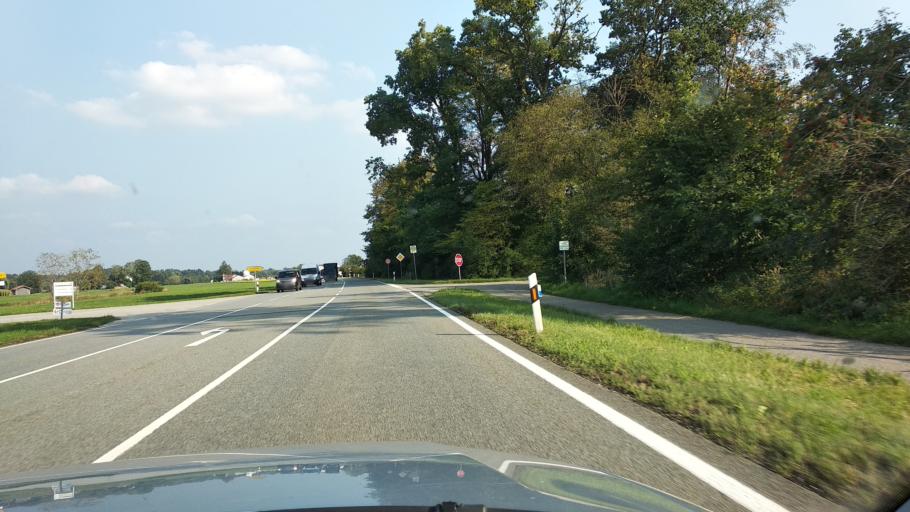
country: DE
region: Bavaria
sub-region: Upper Bavaria
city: Edling
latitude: 48.0686
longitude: 12.1491
